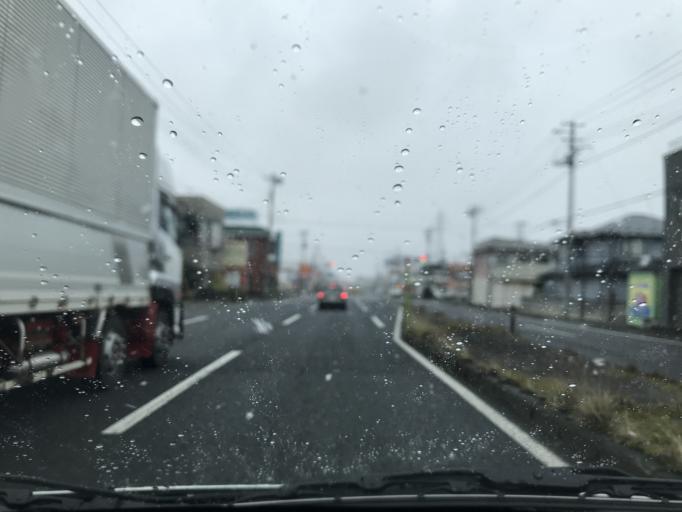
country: JP
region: Iwate
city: Kitakami
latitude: 39.2900
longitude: 141.1045
